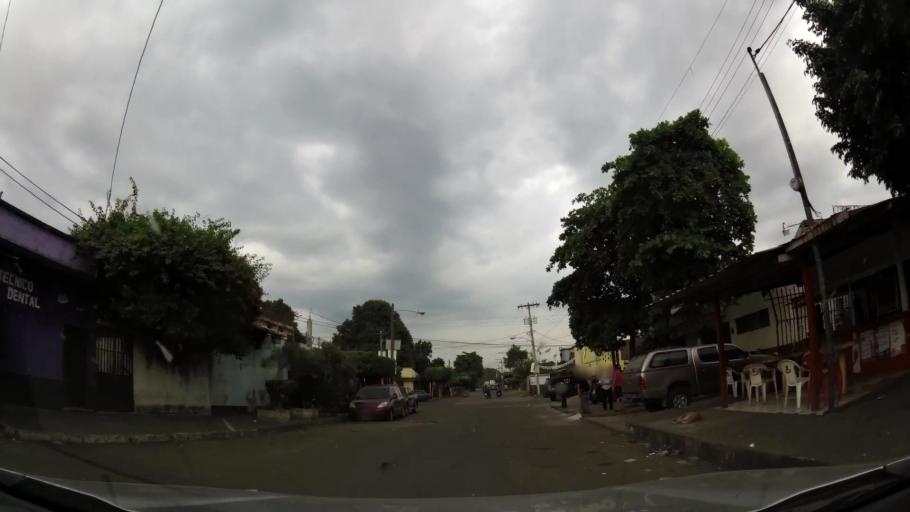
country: GT
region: Escuintla
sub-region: Municipio de Escuintla
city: Escuintla
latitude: 14.2882
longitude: -90.7818
